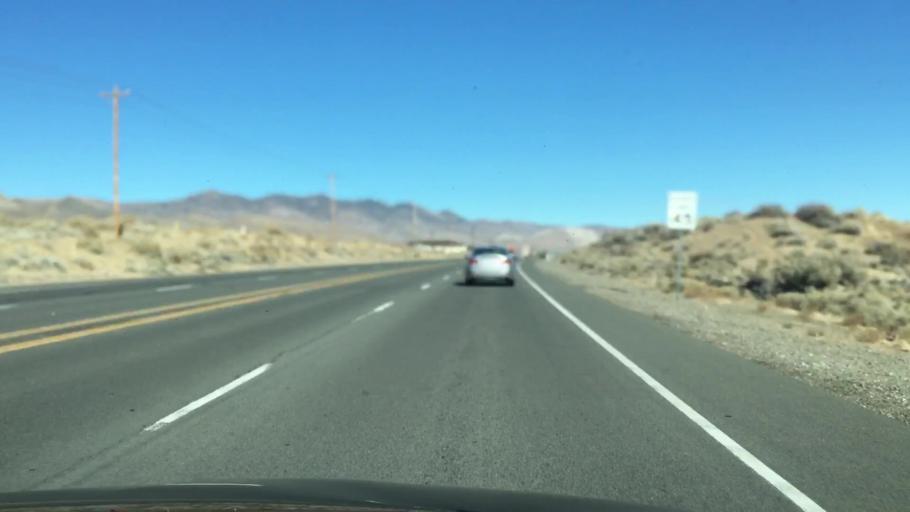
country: US
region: Nevada
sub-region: Lyon County
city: Dayton
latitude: 39.2562
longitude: -119.5859
